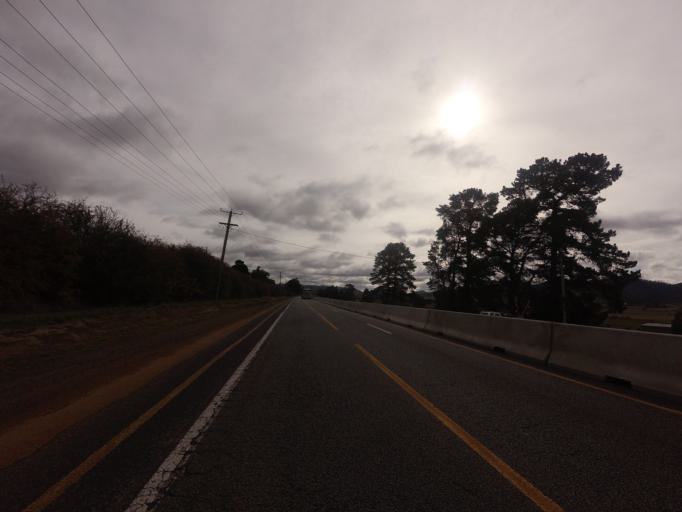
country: AU
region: Tasmania
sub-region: Brighton
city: Bridgewater
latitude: -42.6688
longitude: 147.2545
